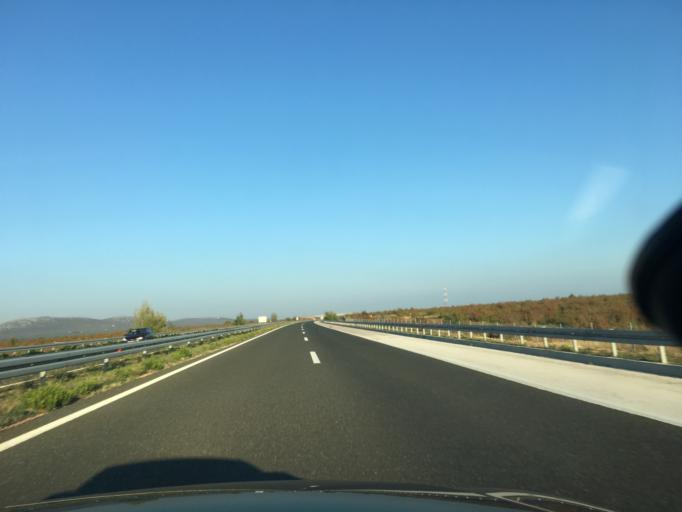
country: HR
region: Sibensko-Kniniska
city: Zaton
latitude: 43.9031
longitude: 15.7691
